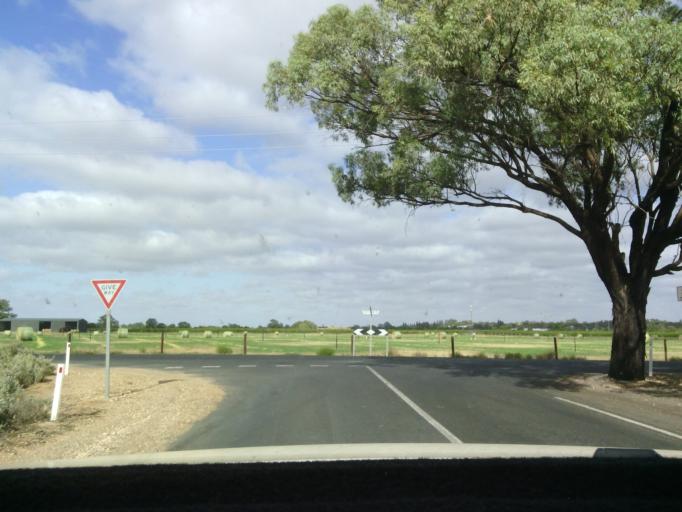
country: AU
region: South Australia
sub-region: Berri and Barmera
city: Berri
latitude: -34.2809
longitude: 140.6263
